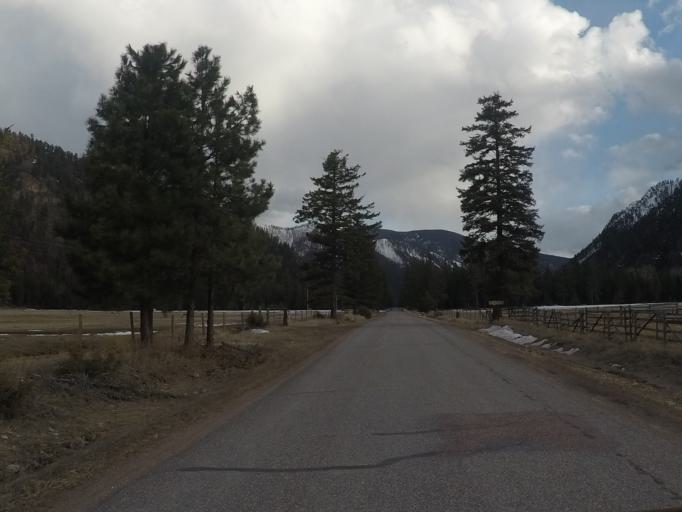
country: US
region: Montana
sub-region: Missoula County
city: Clinton
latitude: 46.6532
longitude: -113.6554
